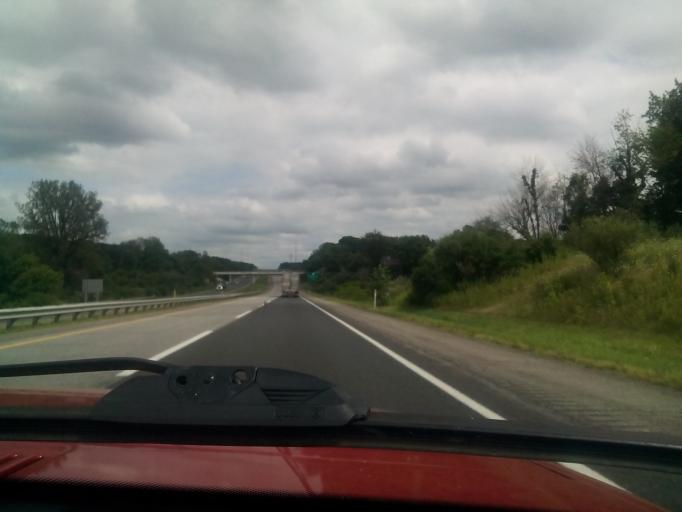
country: US
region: Indiana
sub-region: LaPorte County
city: Westville
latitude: 41.5880
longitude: -86.9125
